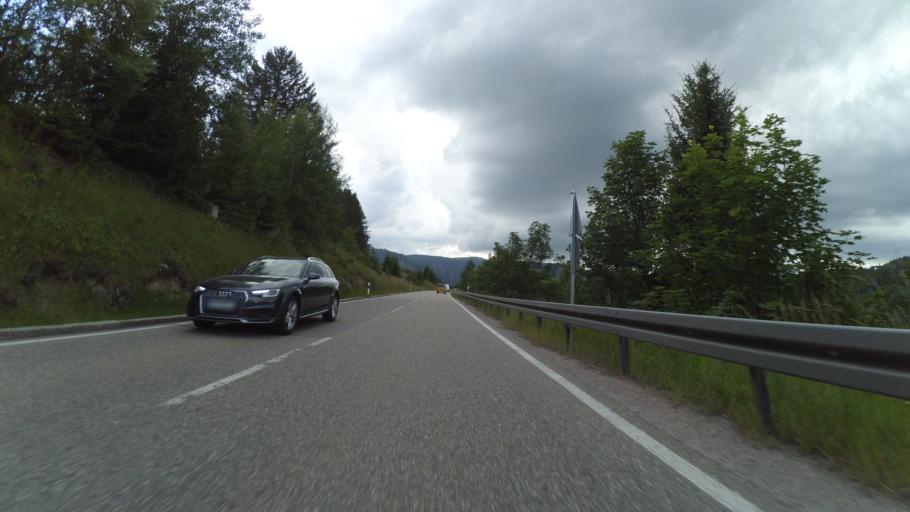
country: DE
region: Baden-Wuerttemberg
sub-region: Freiburg Region
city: Hinterzarten
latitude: 47.8736
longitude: 8.1049
